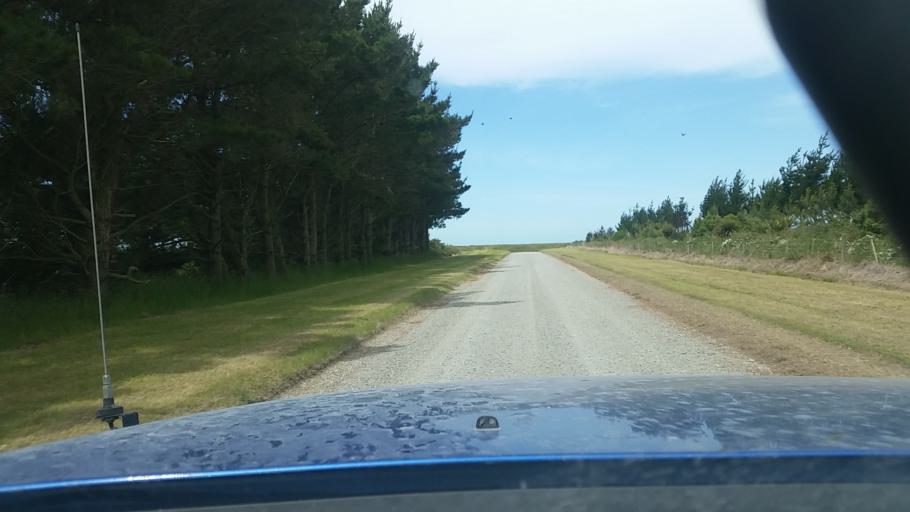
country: NZ
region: Canterbury
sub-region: Ashburton District
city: Tinwald
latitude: -44.0546
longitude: 171.7909
